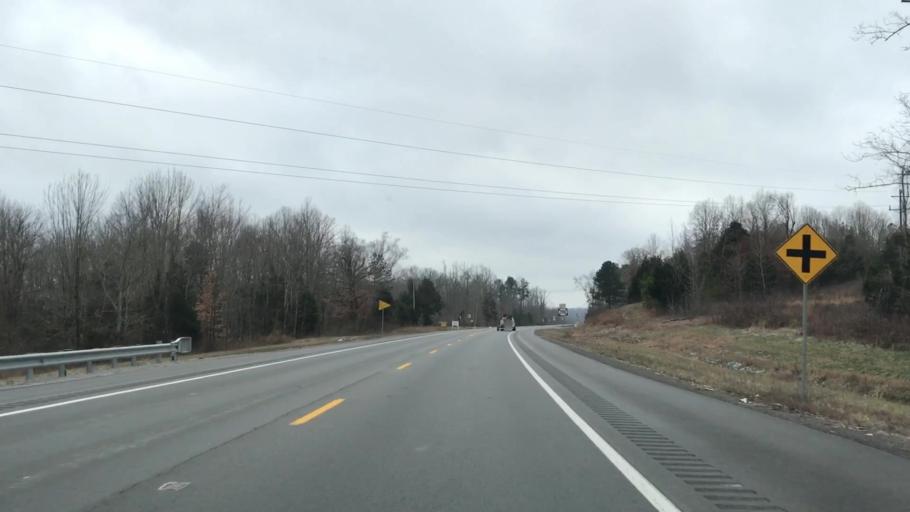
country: US
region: Kentucky
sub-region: Adair County
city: Columbia
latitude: 37.0507
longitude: -85.3625
